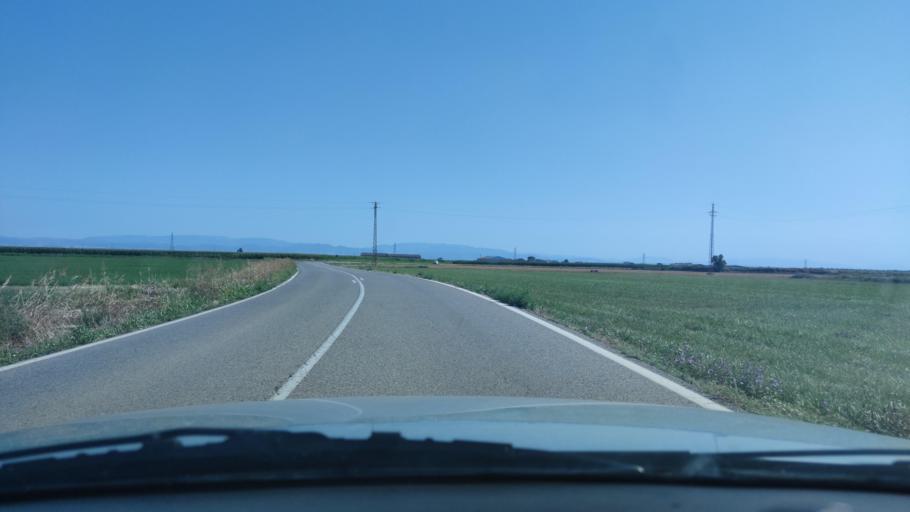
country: ES
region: Catalonia
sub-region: Provincia de Lleida
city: Bellvis
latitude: 41.6414
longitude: 0.7945
